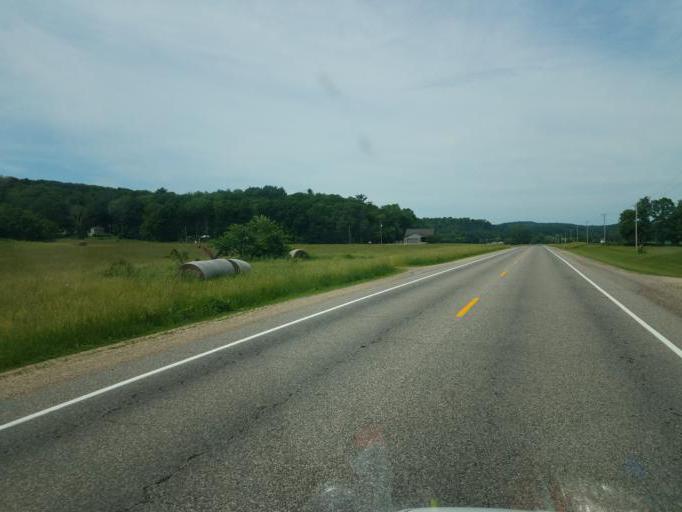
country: US
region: Wisconsin
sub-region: Juneau County
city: Mauston
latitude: 43.7891
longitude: -90.1544
